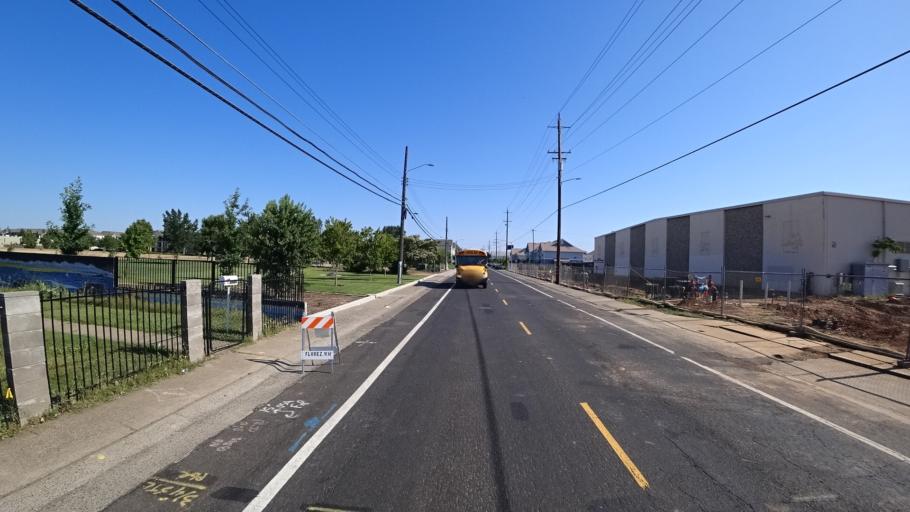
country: US
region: California
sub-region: Sacramento County
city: Florin
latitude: 38.5456
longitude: -121.4232
